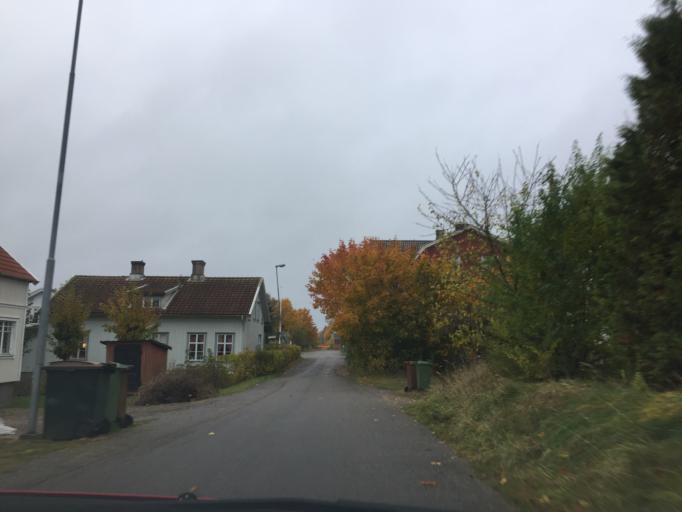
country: SE
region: Vaestra Goetaland
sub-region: Trollhattan
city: Sjuntorp
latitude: 58.1577
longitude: 12.3053
